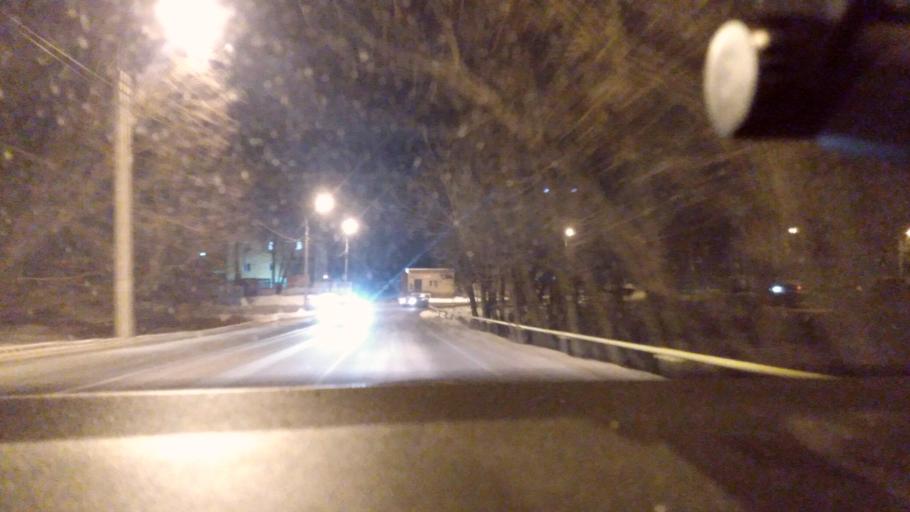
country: RU
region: Moskovskaya
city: Zheleznodorozhnyy
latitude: 55.7361
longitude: 38.0408
